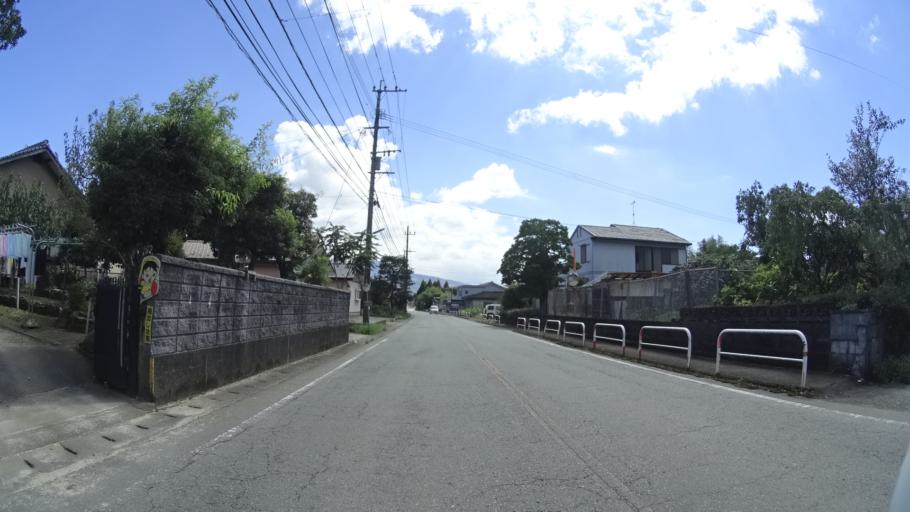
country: JP
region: Kumamoto
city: Aso
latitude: 32.9670
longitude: 131.0358
